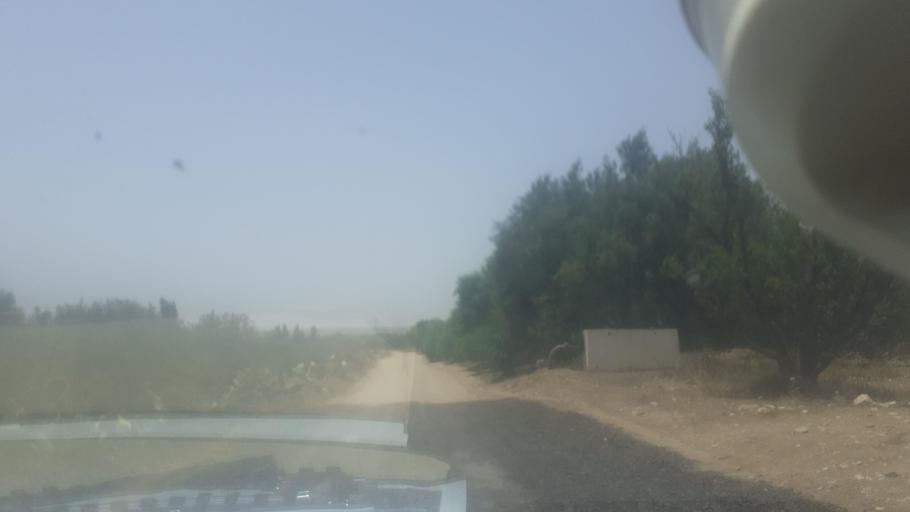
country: TN
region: Al Qasrayn
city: Kasserine
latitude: 35.2188
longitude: 8.8814
